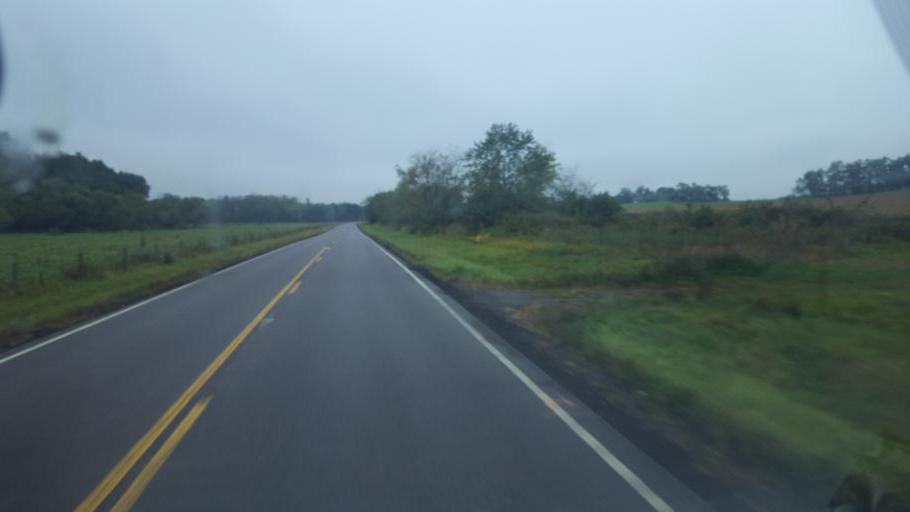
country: US
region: Ohio
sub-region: Sandusky County
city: Bellville
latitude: 40.5435
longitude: -82.4903
